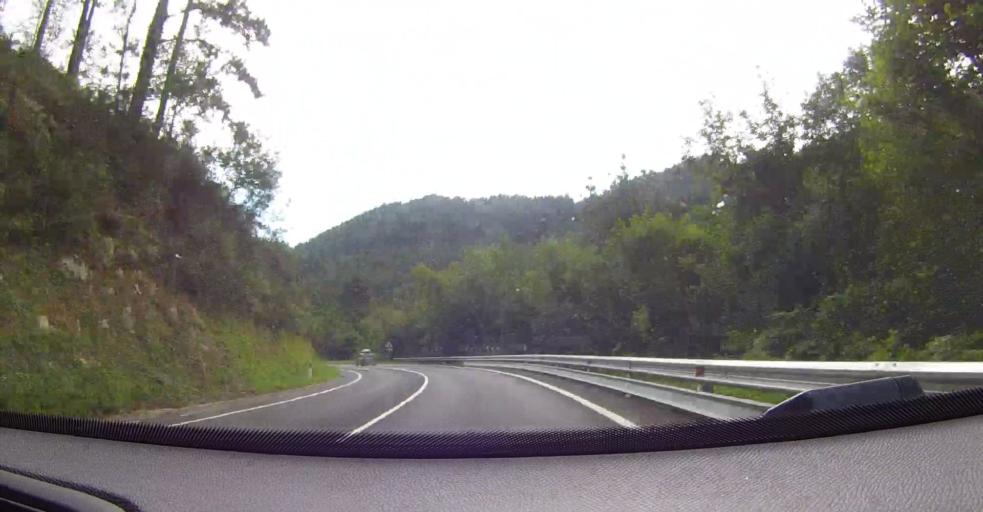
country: ES
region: Basque Country
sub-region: Bizkaia
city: Ibarrangelu
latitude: 43.3780
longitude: -2.6349
